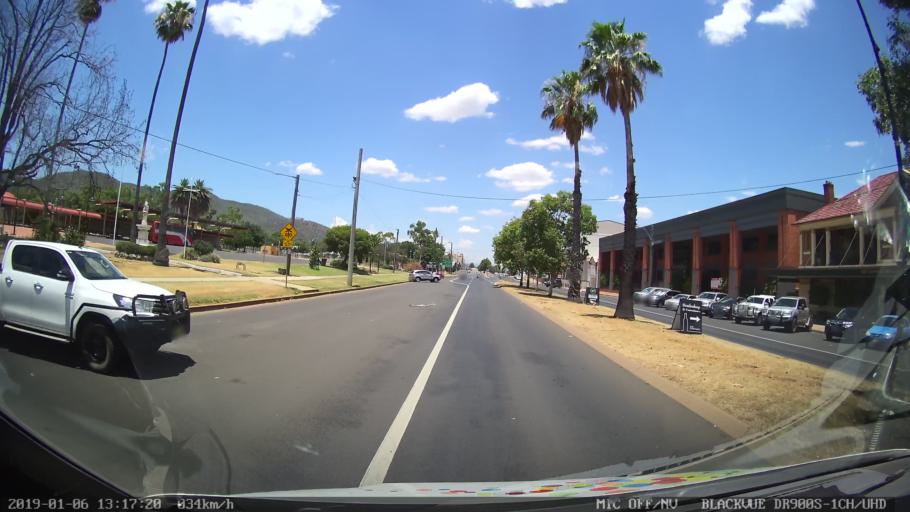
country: AU
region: New South Wales
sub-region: Tamworth Municipality
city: Tamworth
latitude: -31.0876
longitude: 150.9302
